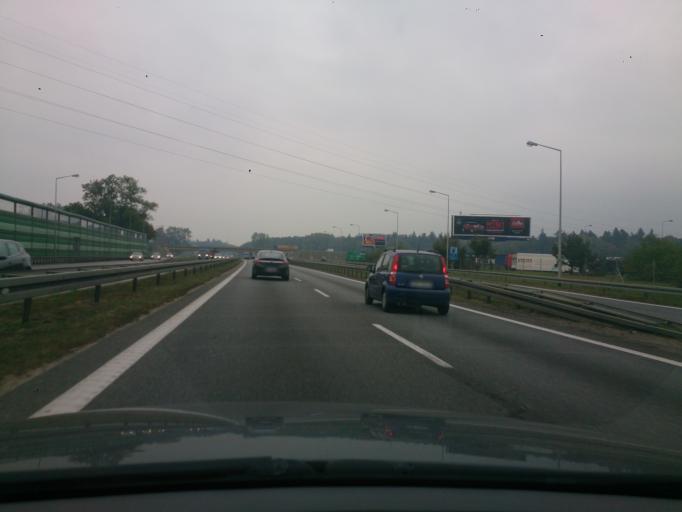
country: PL
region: Pomeranian Voivodeship
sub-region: Gdynia
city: Wielki Kack
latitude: 54.4257
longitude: 18.4881
